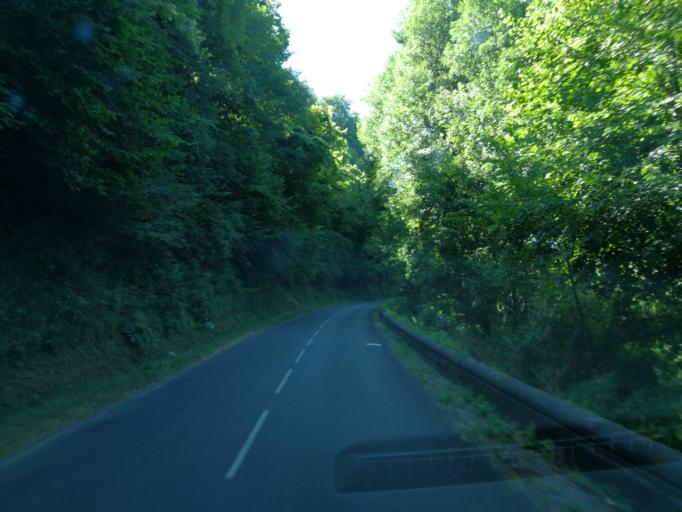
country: FR
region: Midi-Pyrenees
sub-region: Departement du Lot
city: Souillac
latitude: 44.8670
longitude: 1.4216
